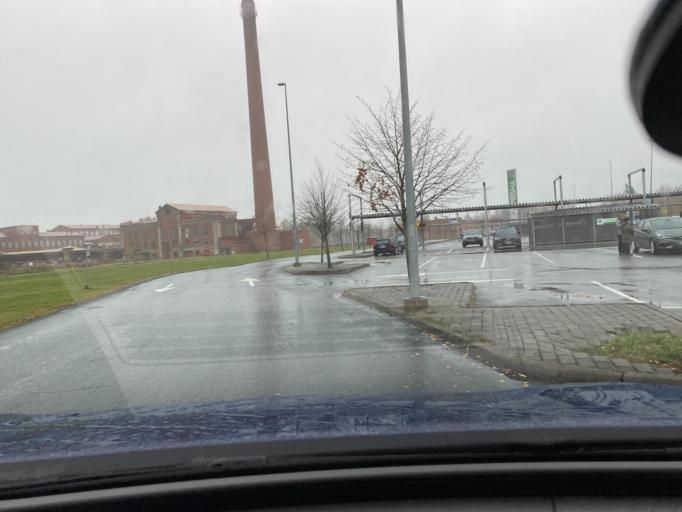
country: FI
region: Haeme
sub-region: Forssa
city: Forssa
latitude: 60.8111
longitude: 23.6377
